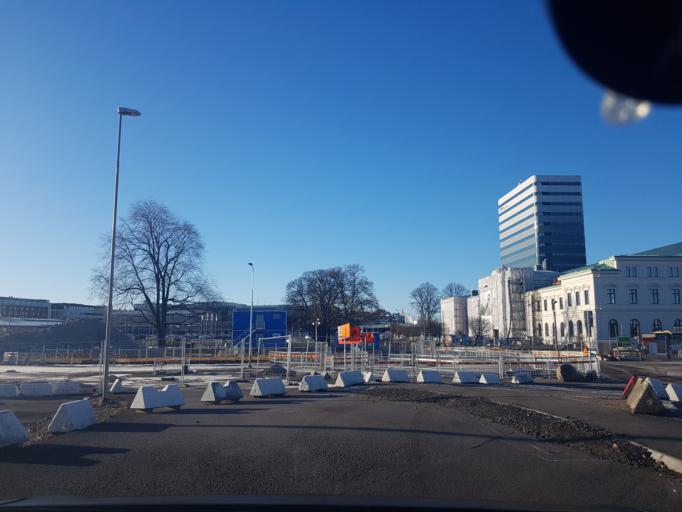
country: SE
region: Vaestra Goetaland
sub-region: Goteborg
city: Goeteborg
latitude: 57.7126
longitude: 11.9759
